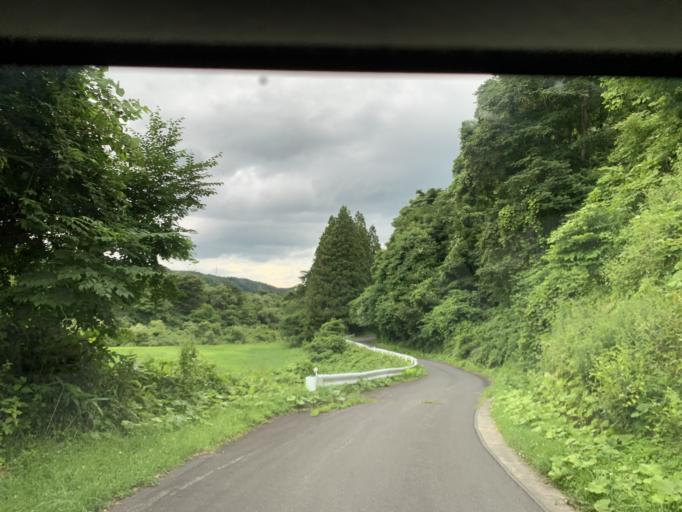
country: JP
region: Iwate
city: Ichinoseki
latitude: 38.9613
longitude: 141.0035
